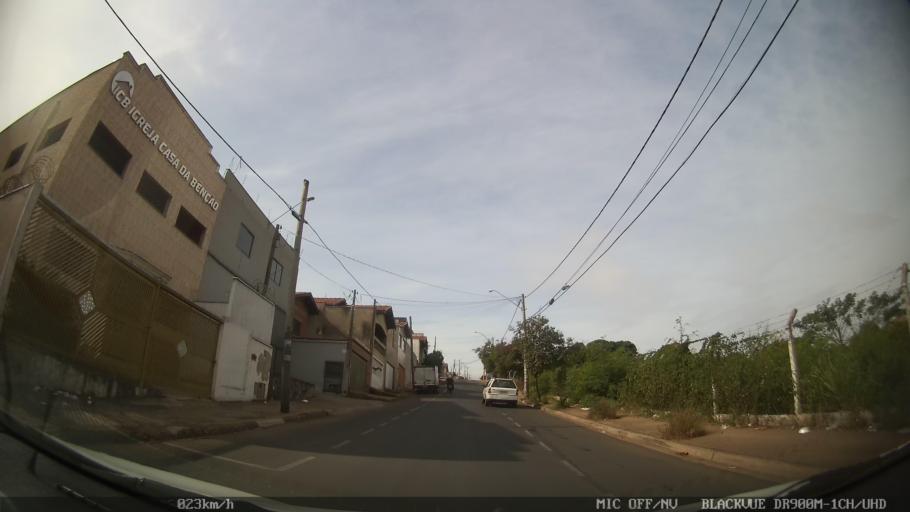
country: BR
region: Sao Paulo
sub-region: Piracicaba
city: Piracicaba
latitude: -22.7403
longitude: -47.6646
